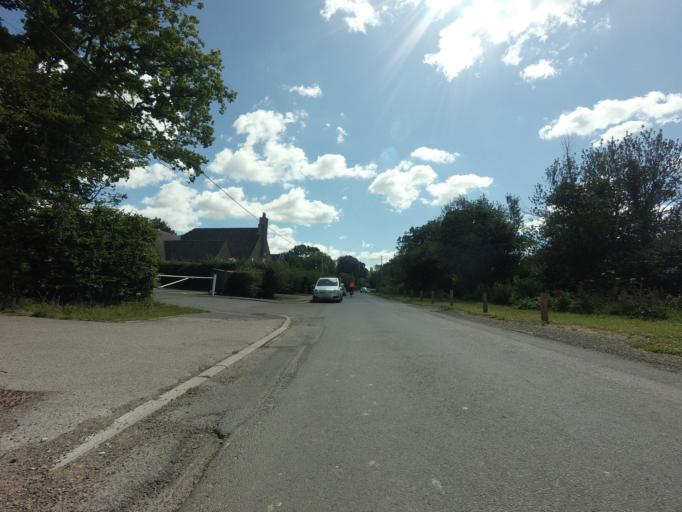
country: GB
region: England
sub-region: East Sussex
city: Horam
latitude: 50.8999
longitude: 0.1931
